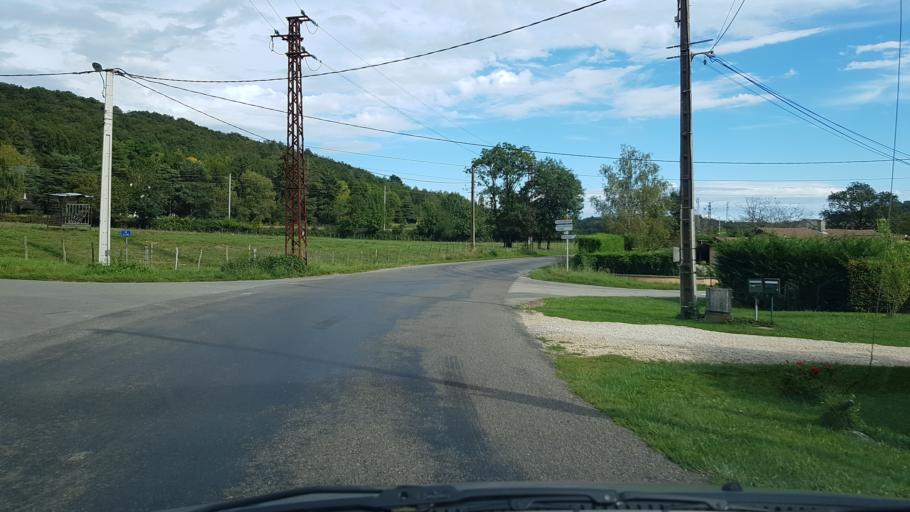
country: FR
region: Rhone-Alpes
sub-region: Departement de l'Ain
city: Ceyzeriat
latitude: 46.1613
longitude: 5.3448
